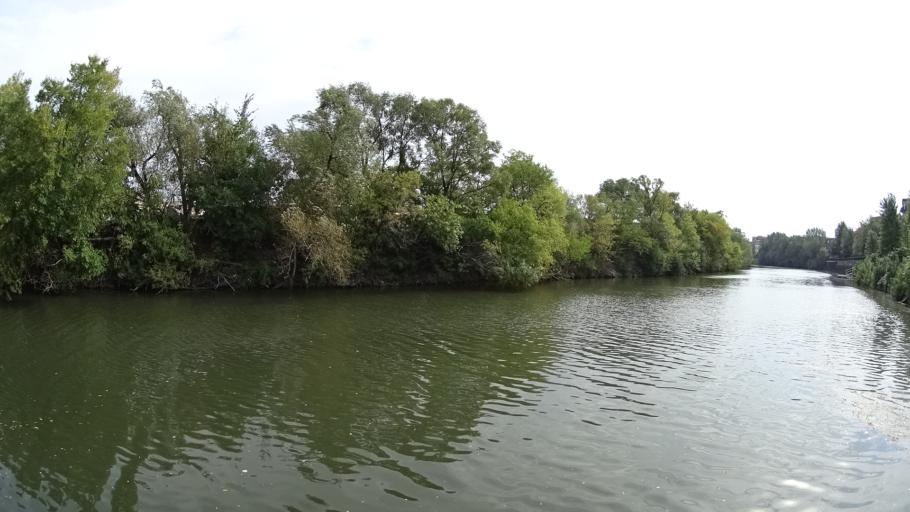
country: US
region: Illinois
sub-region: Cook County
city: Lincolnwood
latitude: 41.9357
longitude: -87.6877
